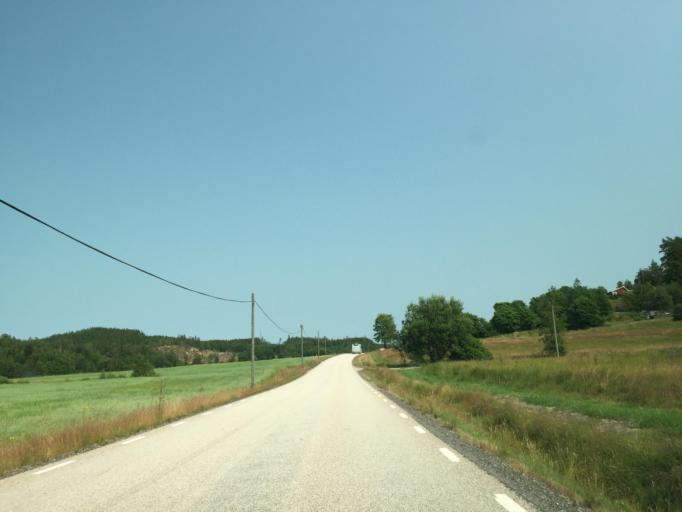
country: SE
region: Vaestra Goetaland
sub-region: Lilla Edets Kommun
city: Lilla Edet
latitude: 58.1443
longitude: 12.0142
